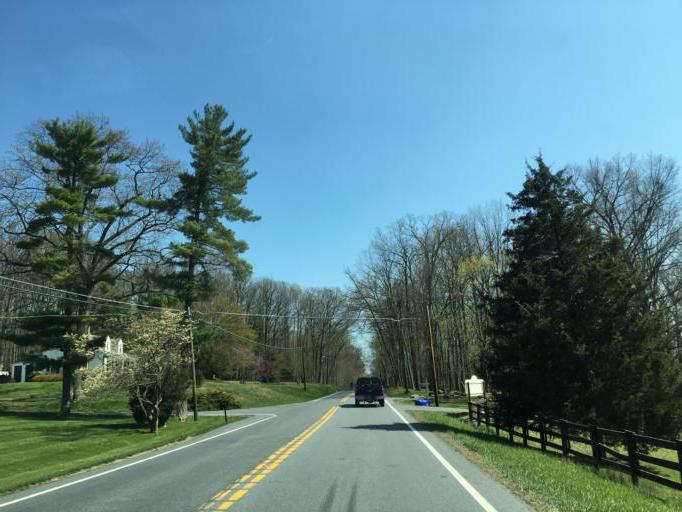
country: US
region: Maryland
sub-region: Frederick County
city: Woodsboro
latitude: 39.5053
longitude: -77.2722
